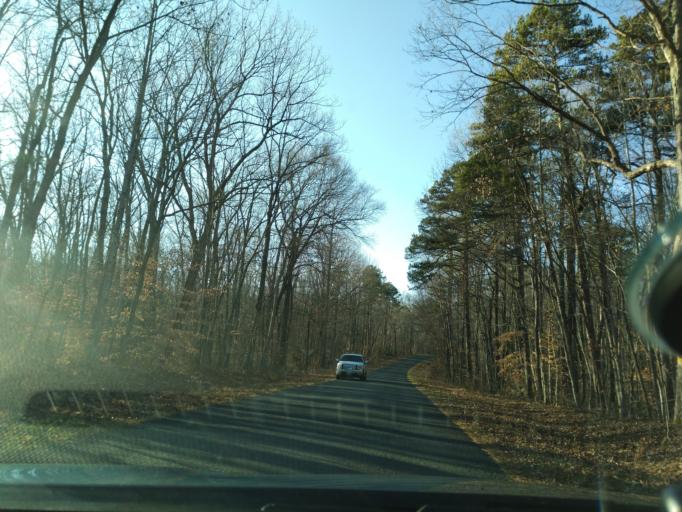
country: US
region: Virginia
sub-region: Appomattox County
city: Appomattox
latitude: 37.3951
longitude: -78.6530
